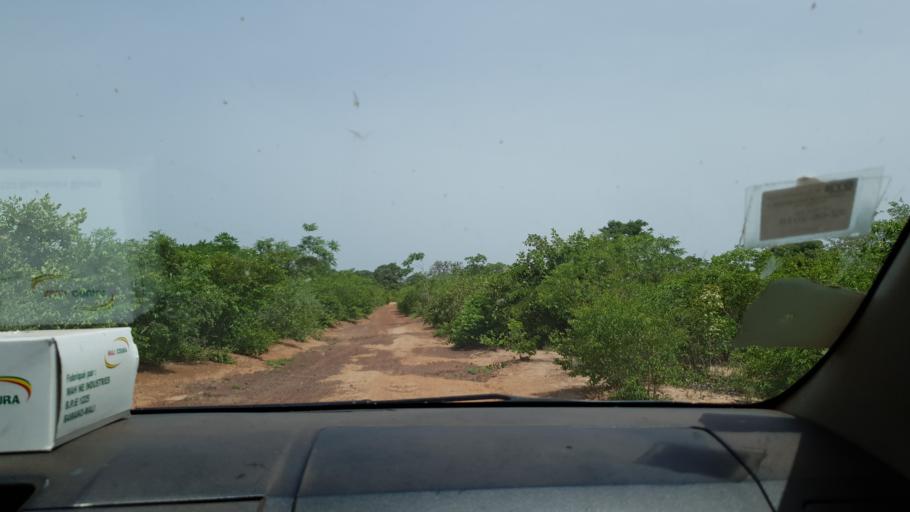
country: ML
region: Koulikoro
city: Koulikoro
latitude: 12.6671
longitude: -7.2394
